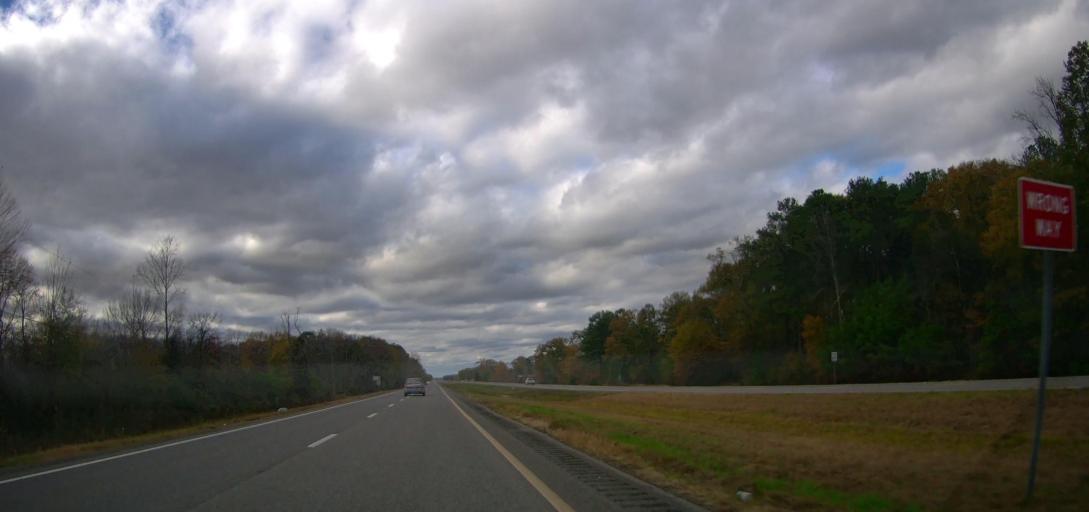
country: US
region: Alabama
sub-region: Morgan County
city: Danville
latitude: 34.4212
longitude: -87.1706
